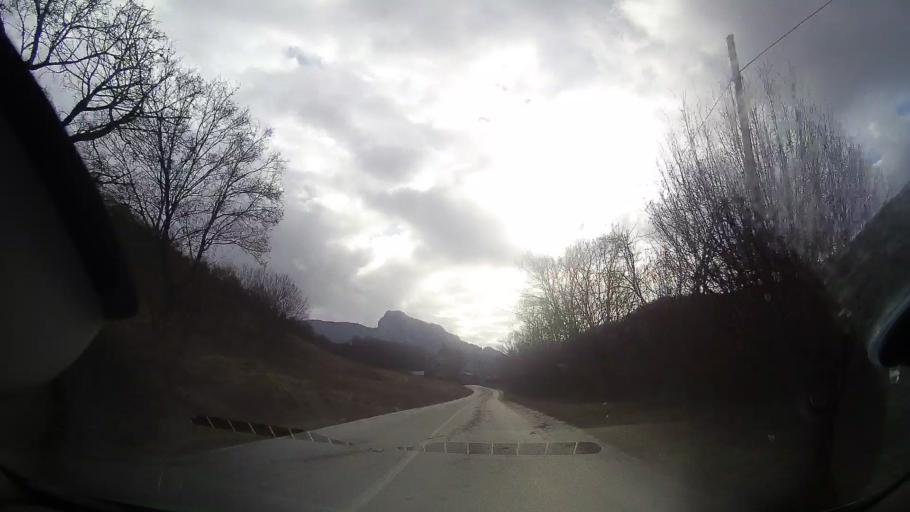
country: RO
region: Alba
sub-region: Comuna Rimetea
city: Rimetea
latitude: 46.4866
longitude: 23.5811
